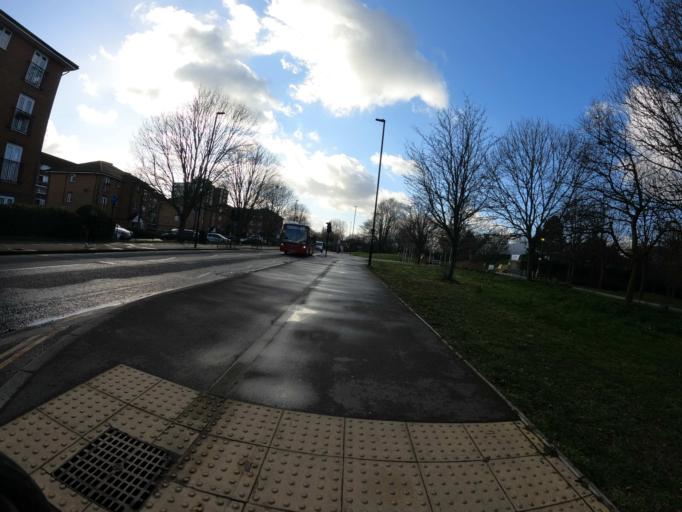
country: GB
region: England
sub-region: Greater London
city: Greenford
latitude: 51.5287
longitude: -0.3303
